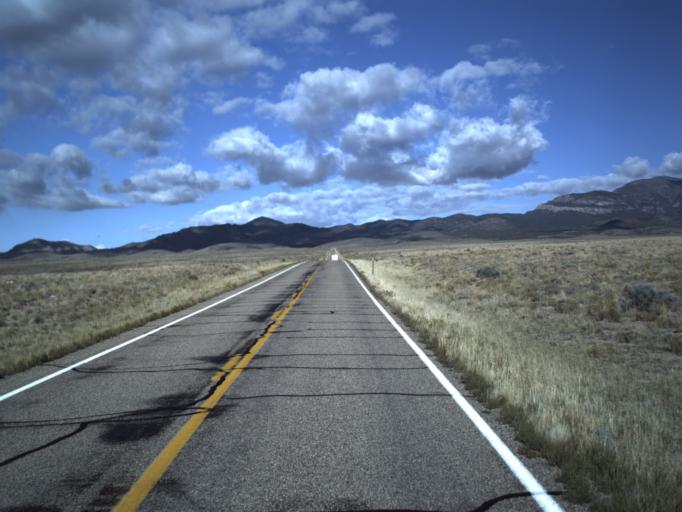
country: US
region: Utah
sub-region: Beaver County
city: Milford
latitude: 38.4434
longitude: -113.1746
